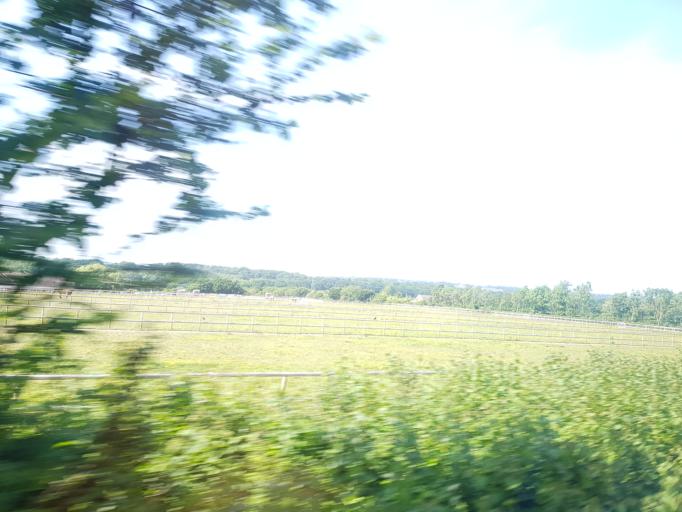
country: GB
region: England
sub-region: Isle of Wight
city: Newport
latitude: 50.7080
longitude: -1.2595
